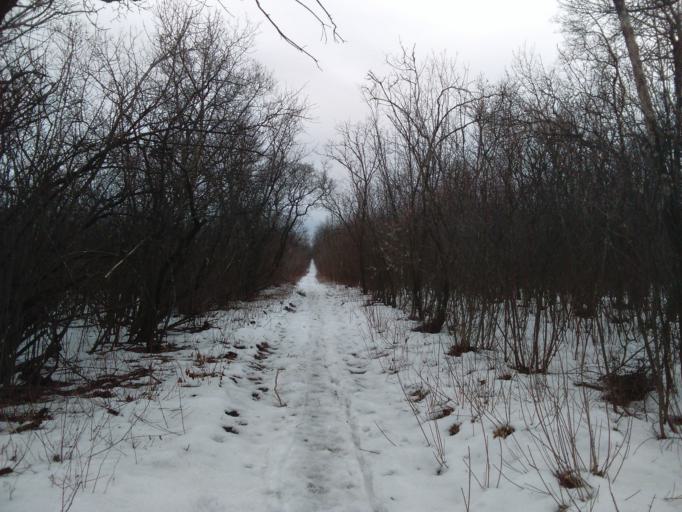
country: RU
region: Rostov
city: Temernik
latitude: 47.3540
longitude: 39.7399
